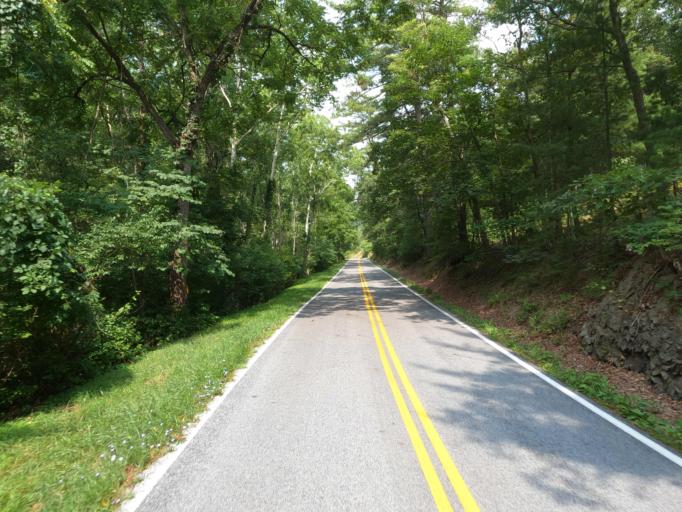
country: US
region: West Virginia
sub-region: Morgan County
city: Berkeley Springs
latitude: 39.6765
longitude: -78.2660
